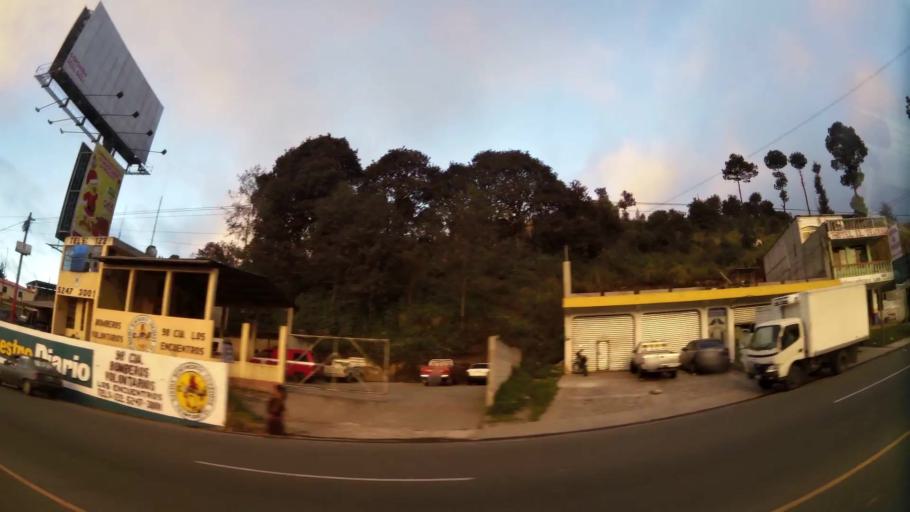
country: GT
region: Solola
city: Concepcion
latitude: 14.8518
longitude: -91.1470
